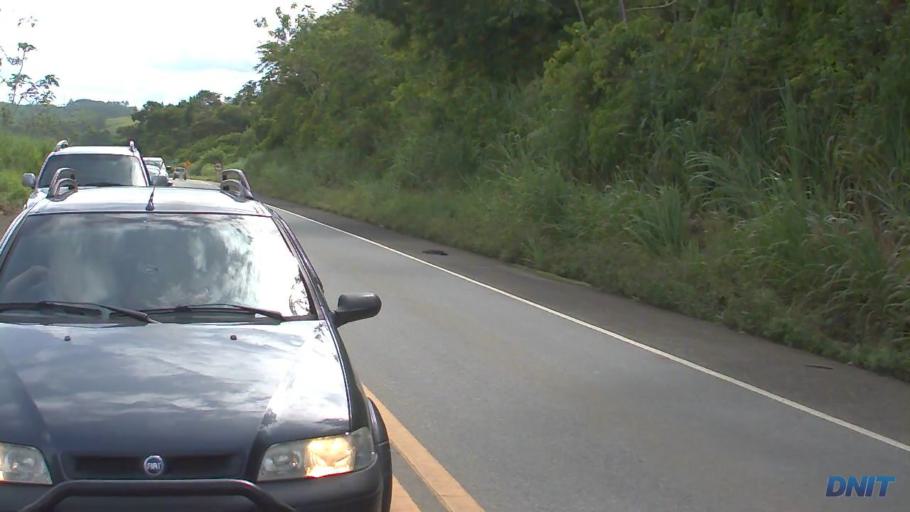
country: BR
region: Minas Gerais
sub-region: Ipaba
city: Ipaba
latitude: -19.3741
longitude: -42.4614
